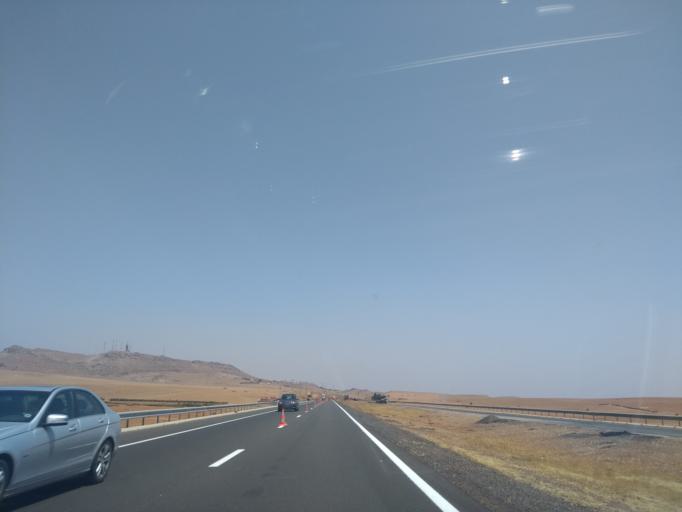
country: MA
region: Marrakech-Tensift-Al Haouz
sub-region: Kelaa-Des-Sraghna
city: Sidi Abdallah
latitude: 32.4526
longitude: -7.9313
